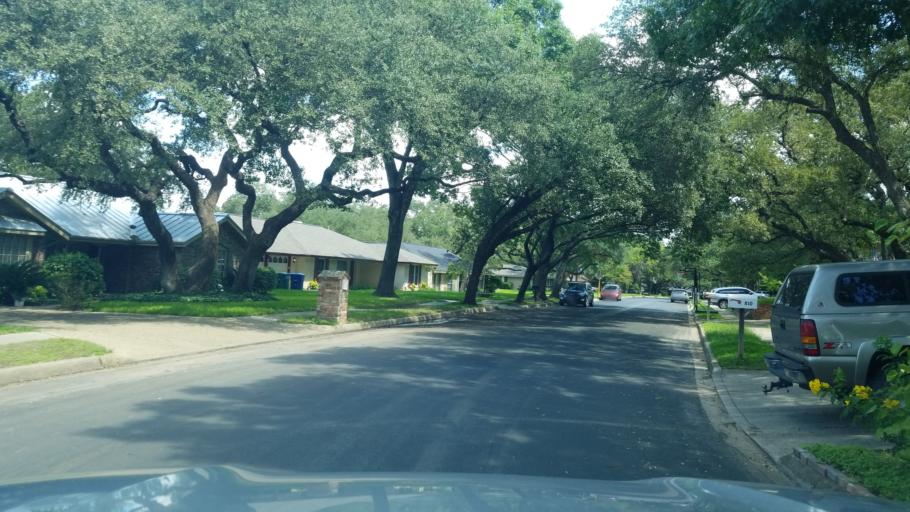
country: US
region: Texas
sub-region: Bexar County
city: Castle Hills
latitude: 29.5462
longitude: -98.5059
